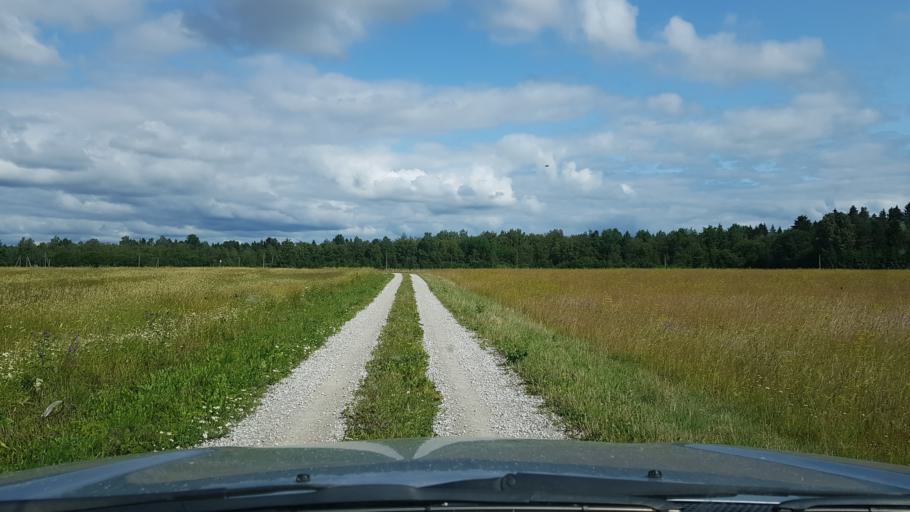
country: EE
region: Ida-Virumaa
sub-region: Narva-Joesuu linn
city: Narva-Joesuu
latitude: 59.3700
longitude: 27.9518
